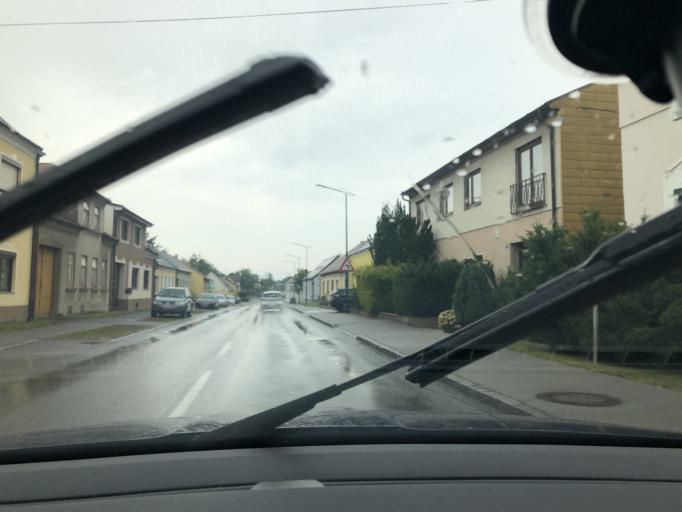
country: AT
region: Lower Austria
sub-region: Politischer Bezirk Ganserndorf
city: Ganserndorf
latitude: 48.3622
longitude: 16.7046
